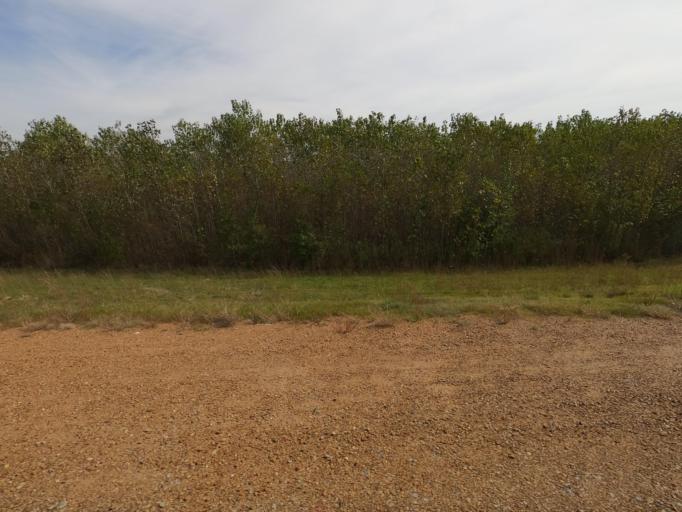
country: US
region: Tennessee
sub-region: Shelby County
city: Arlington
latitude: 35.2924
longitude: -89.6130
